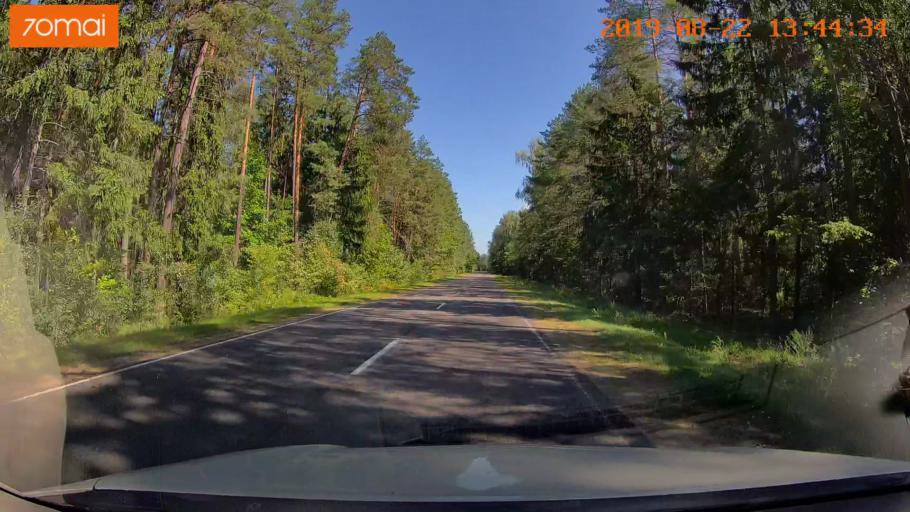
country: BY
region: Mogilev
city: Asipovichy
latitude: 53.2443
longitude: 28.4602
